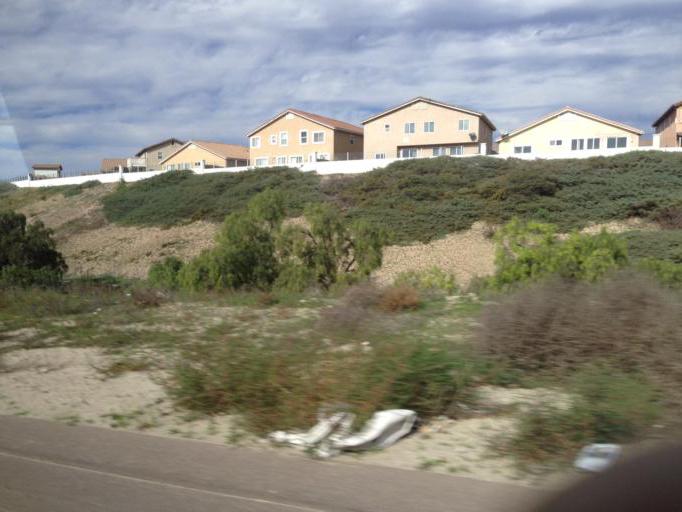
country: MX
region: Baja California
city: Tijuana
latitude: 32.5686
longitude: -117.0364
